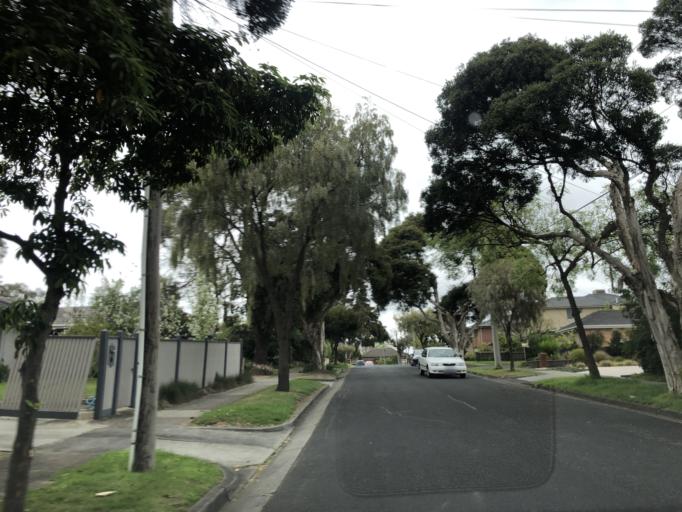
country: AU
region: Victoria
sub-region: Whitehorse
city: Forest Hill
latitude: -37.8378
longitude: 145.1623
